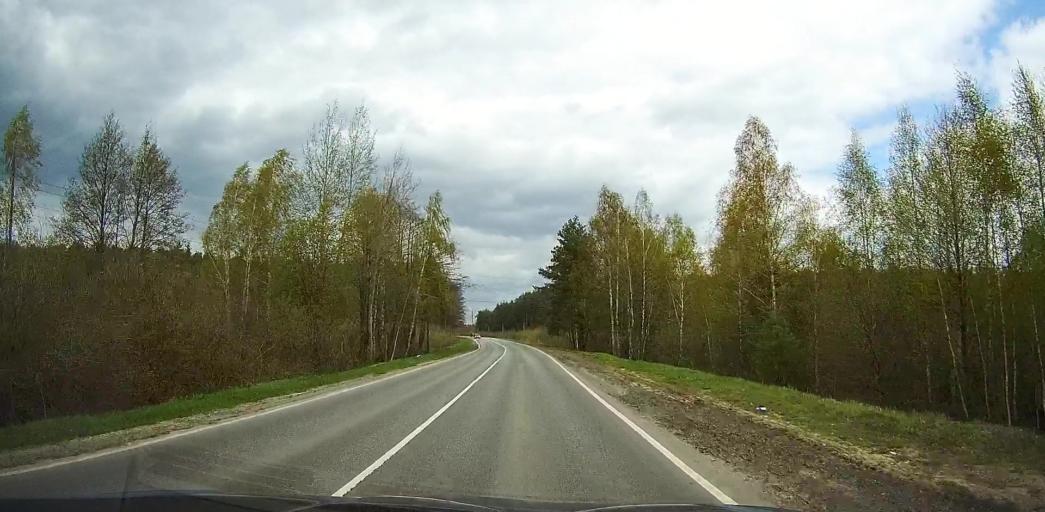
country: RU
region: Moskovskaya
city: Ashitkovo
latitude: 55.4685
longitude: 38.6090
